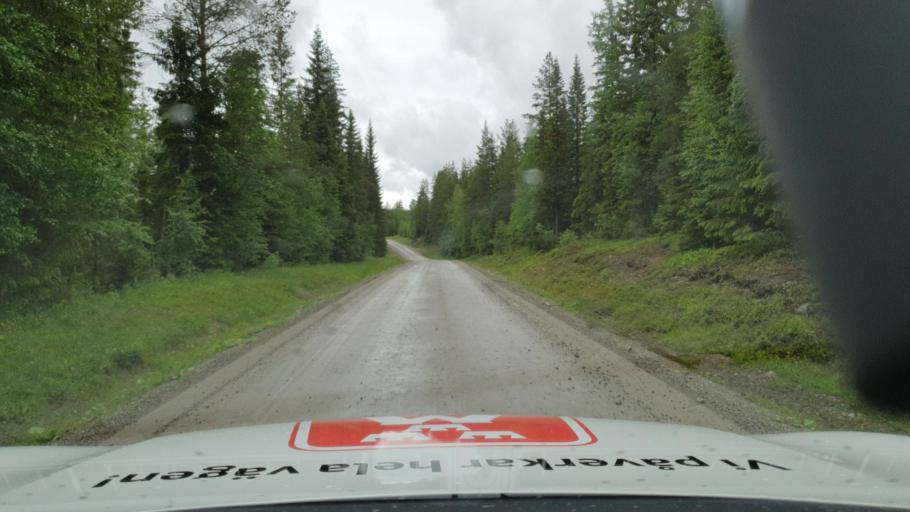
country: SE
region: Vaesterbotten
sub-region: Dorotea Kommun
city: Dorotea
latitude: 64.0559
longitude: 16.7230
